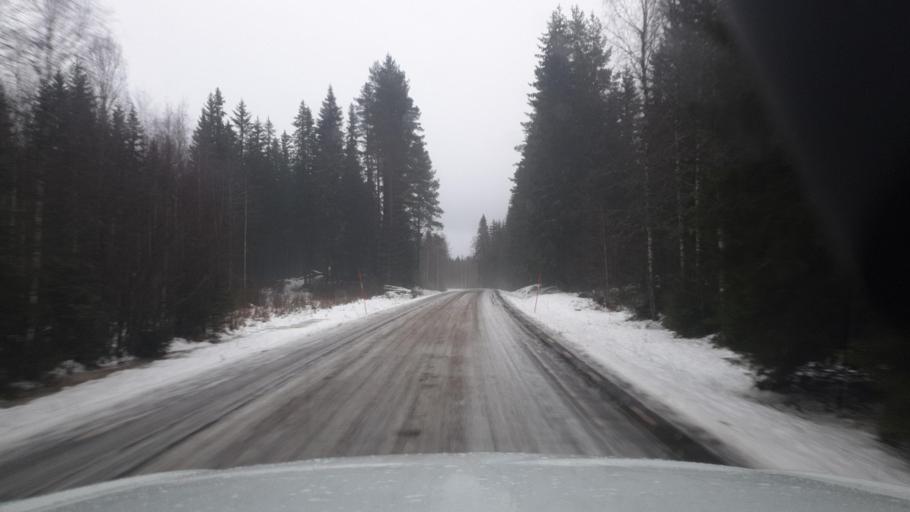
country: SE
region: Vaermland
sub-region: Torsby Kommun
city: Torsby
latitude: 60.0067
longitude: 12.6959
